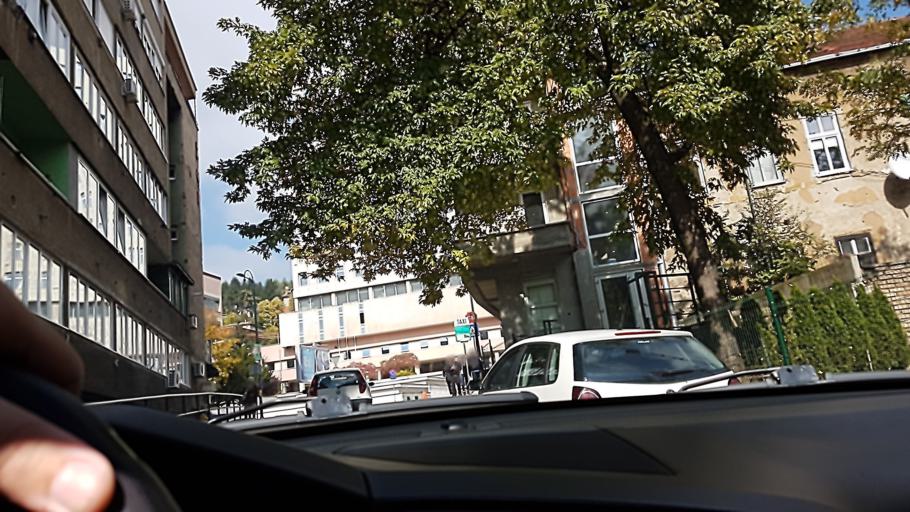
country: BA
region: Federation of Bosnia and Herzegovina
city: Kobilja Glava
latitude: 43.8575
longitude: 18.4083
